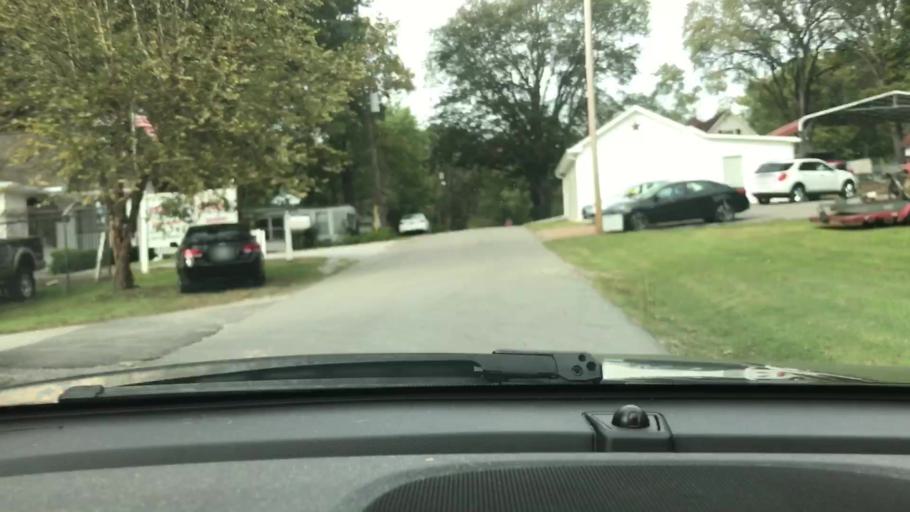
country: US
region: Tennessee
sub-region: Cheatham County
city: Ashland City
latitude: 36.2649
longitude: -87.0580
